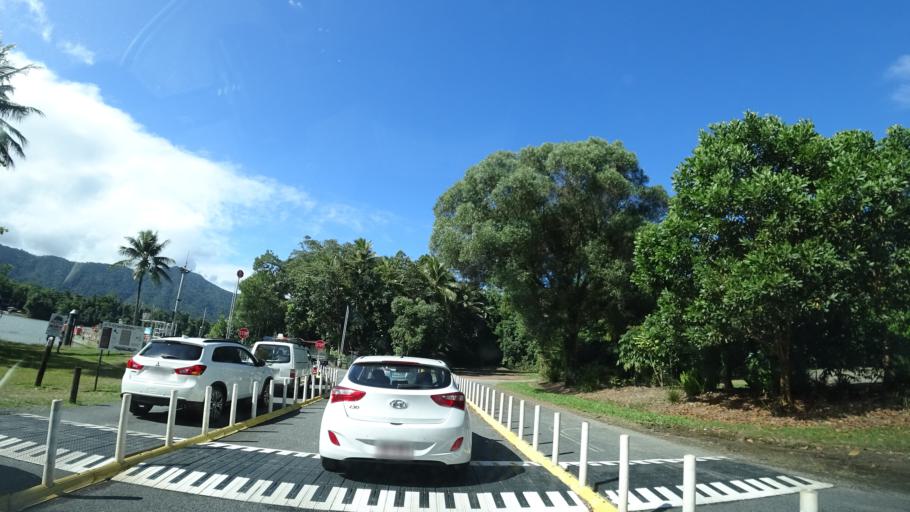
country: AU
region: Queensland
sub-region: Cairns
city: Port Douglas
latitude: -16.2612
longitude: 145.3972
